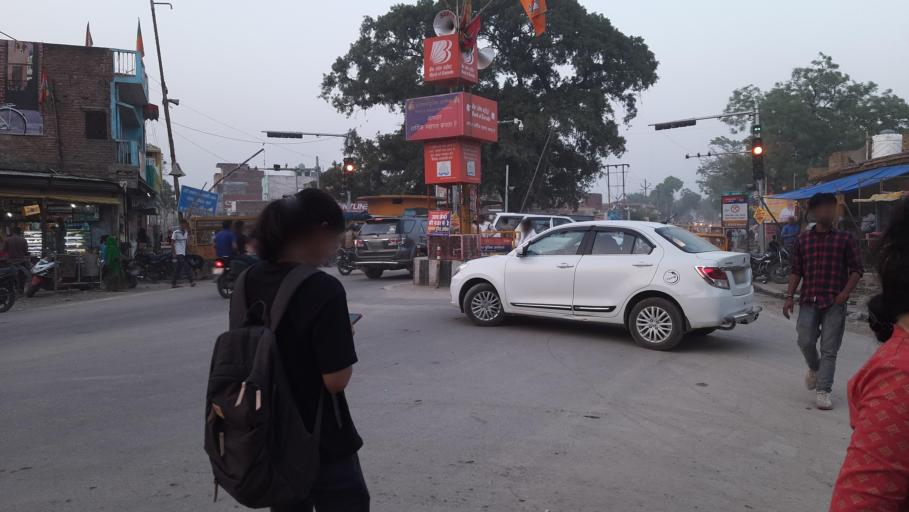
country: IN
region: Uttar Pradesh
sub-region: Faizabad
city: Ayodhya
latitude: 26.7875
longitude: 82.1919
